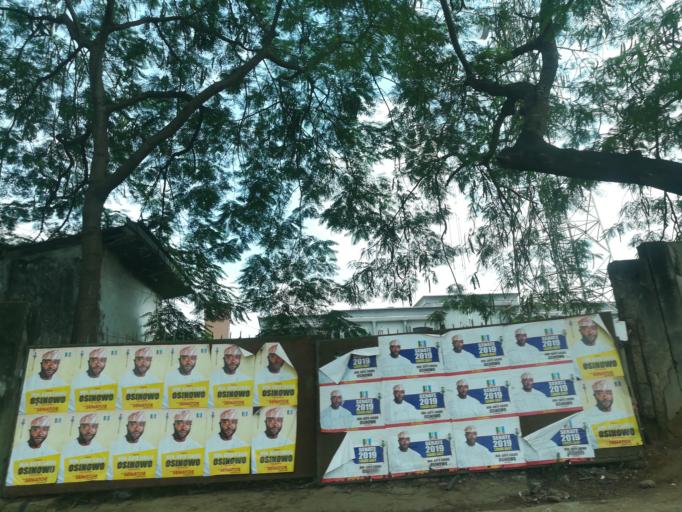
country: NG
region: Lagos
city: Ikorodu
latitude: 6.6129
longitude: 3.5035
